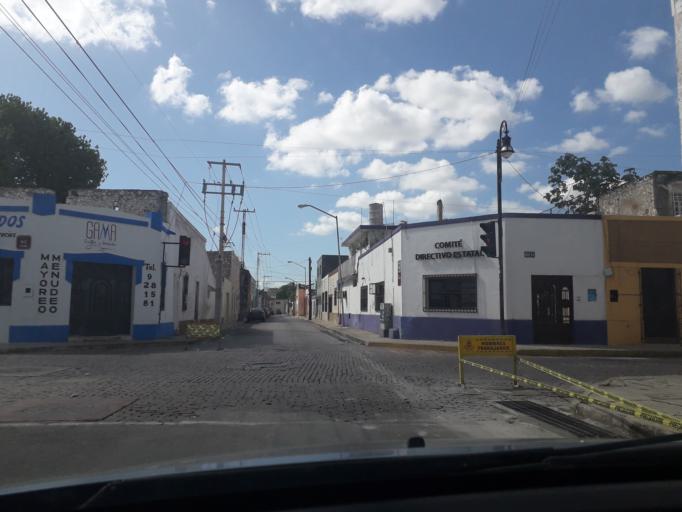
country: MX
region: Yucatan
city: Merida
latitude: 20.9602
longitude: -89.6273
